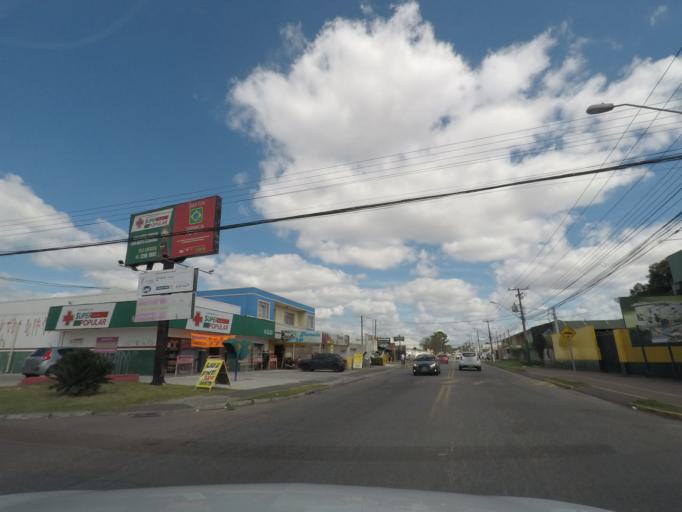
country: BR
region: Parana
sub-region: Sao Jose Dos Pinhais
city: Sao Jose dos Pinhais
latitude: -25.5019
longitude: -49.2231
